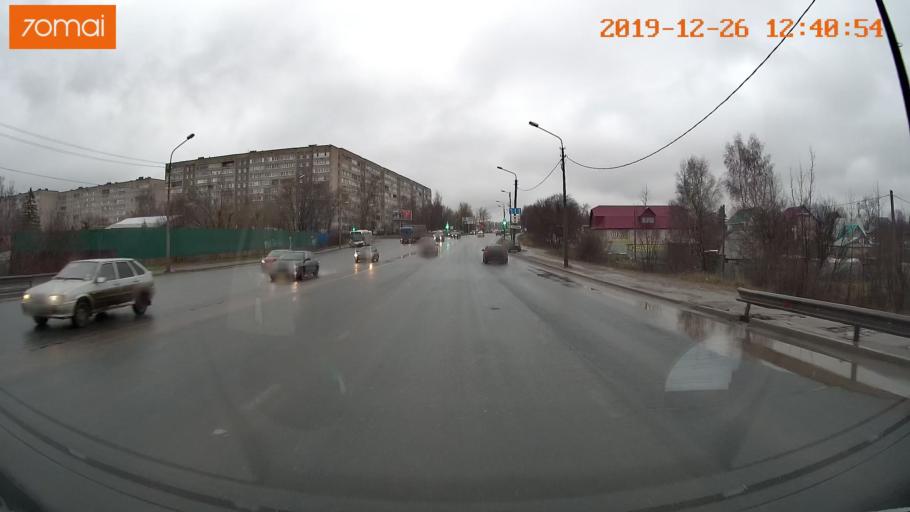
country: RU
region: Vologda
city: Tonshalovo
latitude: 59.1451
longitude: 37.9674
